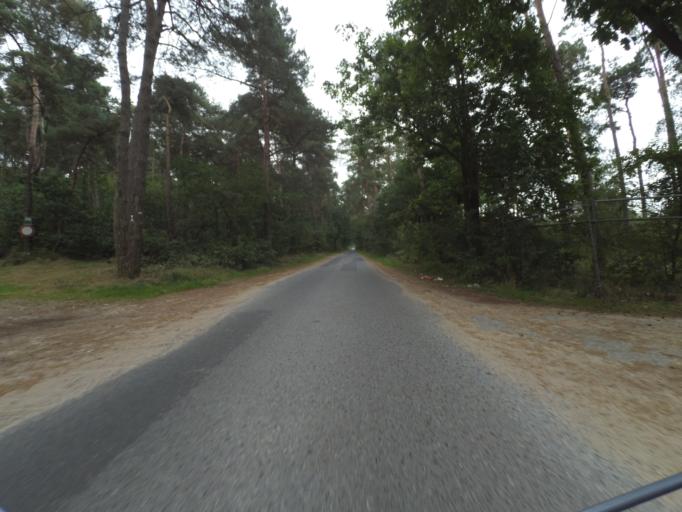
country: NL
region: Overijssel
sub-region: Gemeente Losser
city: Losser
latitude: 52.2818
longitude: 7.0385
